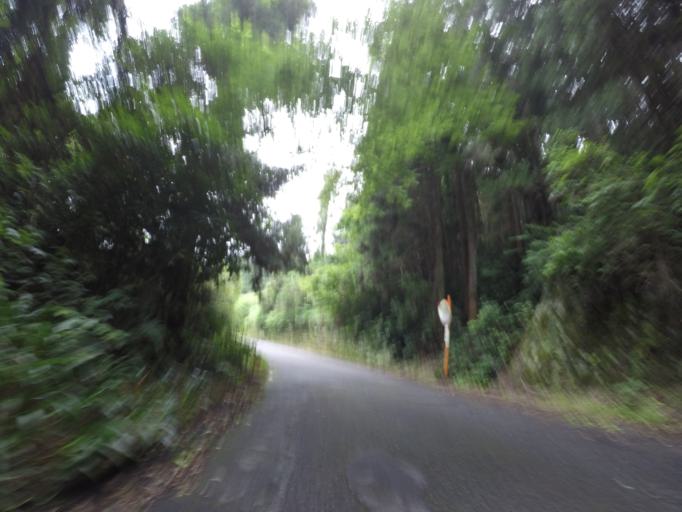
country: JP
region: Shizuoka
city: Fujinomiya
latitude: 35.2335
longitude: 138.5584
